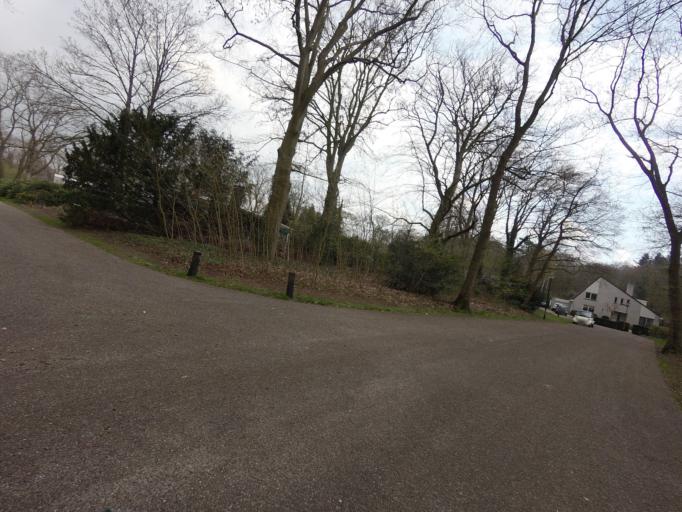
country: NL
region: North Holland
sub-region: Gemeente Naarden
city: Naarden
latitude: 52.2866
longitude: 5.1964
